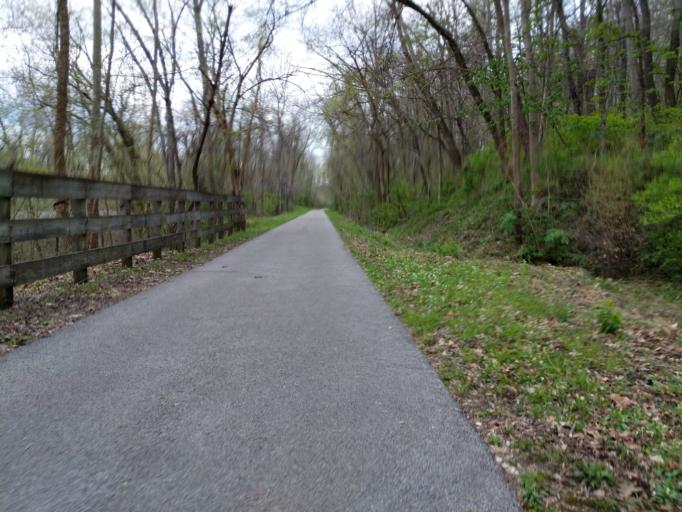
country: US
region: Ohio
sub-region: Athens County
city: The Plains
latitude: 39.3744
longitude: -82.1149
